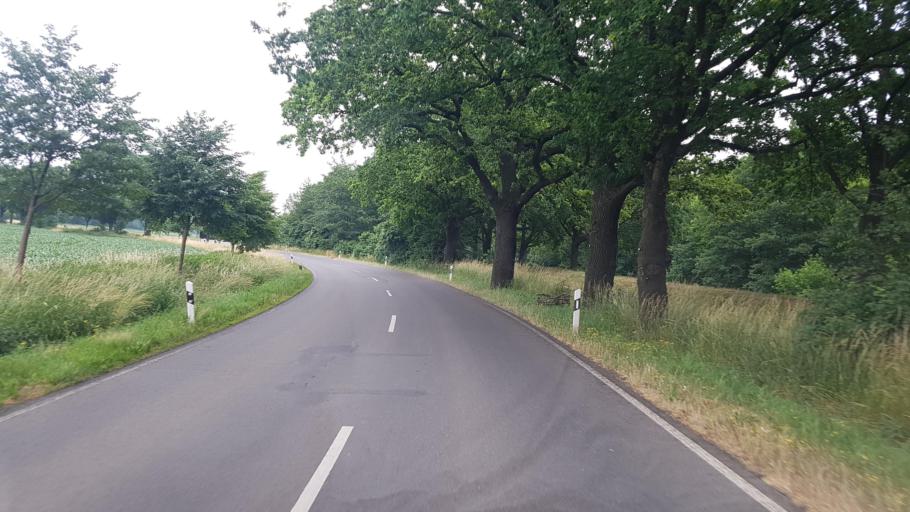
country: DE
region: Brandenburg
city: Schwarzbach
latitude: 51.4792
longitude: 13.9407
